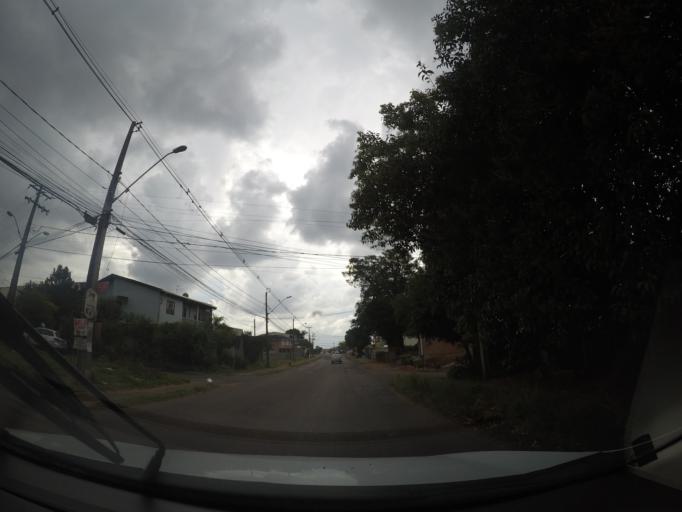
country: BR
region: Parana
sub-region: Sao Jose Dos Pinhais
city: Sao Jose dos Pinhais
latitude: -25.5416
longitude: -49.2418
